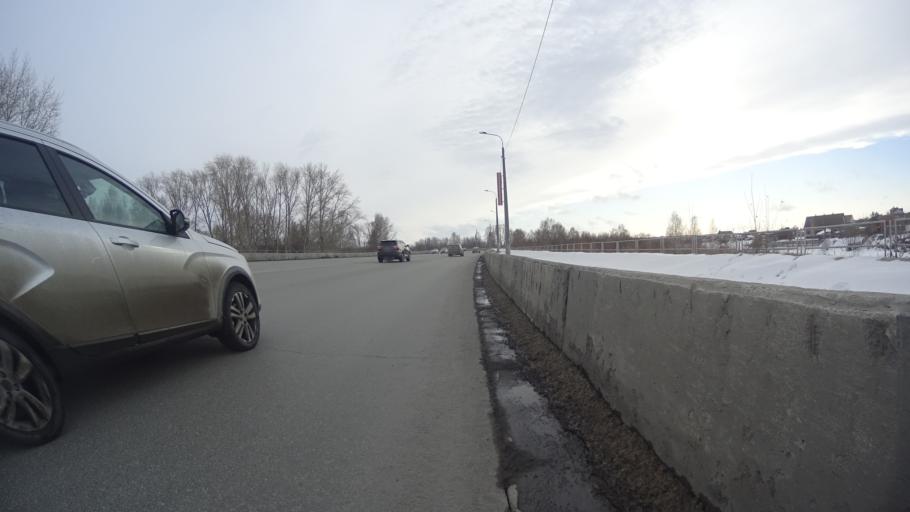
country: RU
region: Chelyabinsk
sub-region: Gorod Chelyabinsk
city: Chelyabinsk
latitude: 55.1521
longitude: 61.3196
